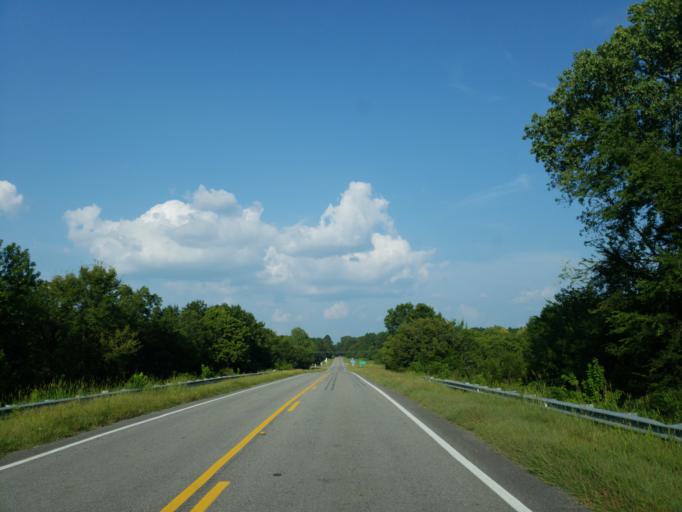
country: US
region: Alabama
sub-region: Greene County
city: Eutaw
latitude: 32.7569
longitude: -88.0213
